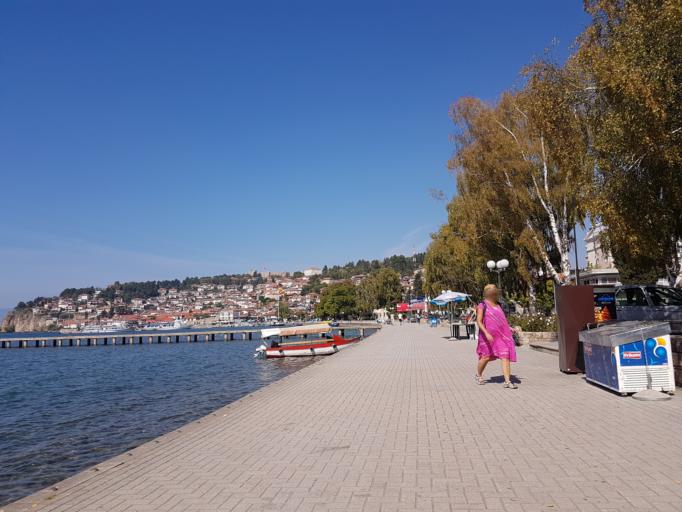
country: MK
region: Ohrid
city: Ohrid
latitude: 41.1106
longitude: 20.8032
